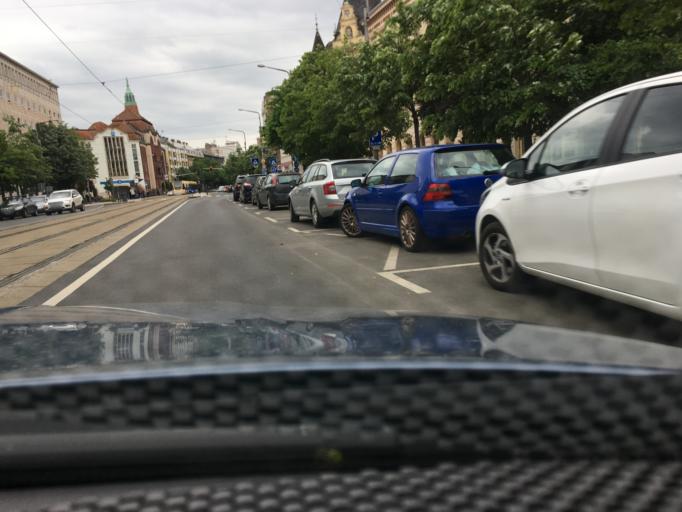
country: HU
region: Hajdu-Bihar
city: Debrecen
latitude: 47.5278
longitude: 21.6258
